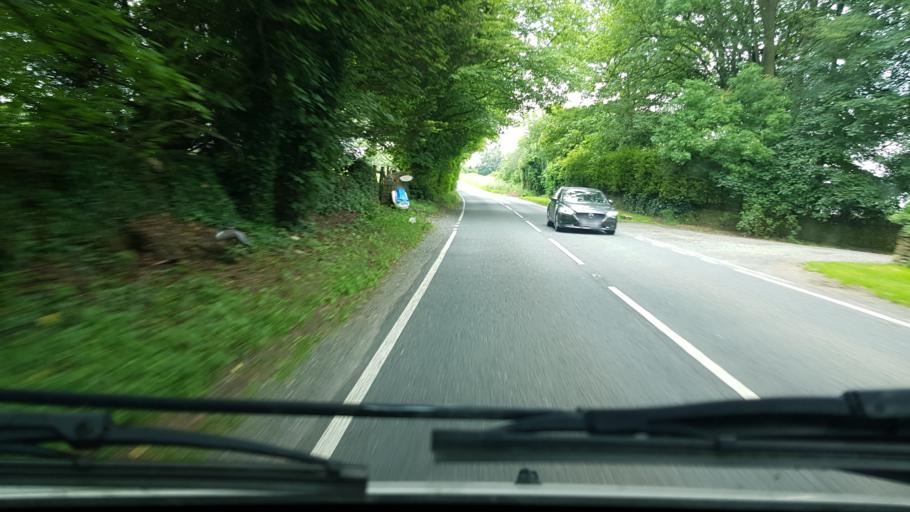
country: GB
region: England
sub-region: Gloucestershire
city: Stow on the Wold
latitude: 51.9391
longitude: -1.7283
